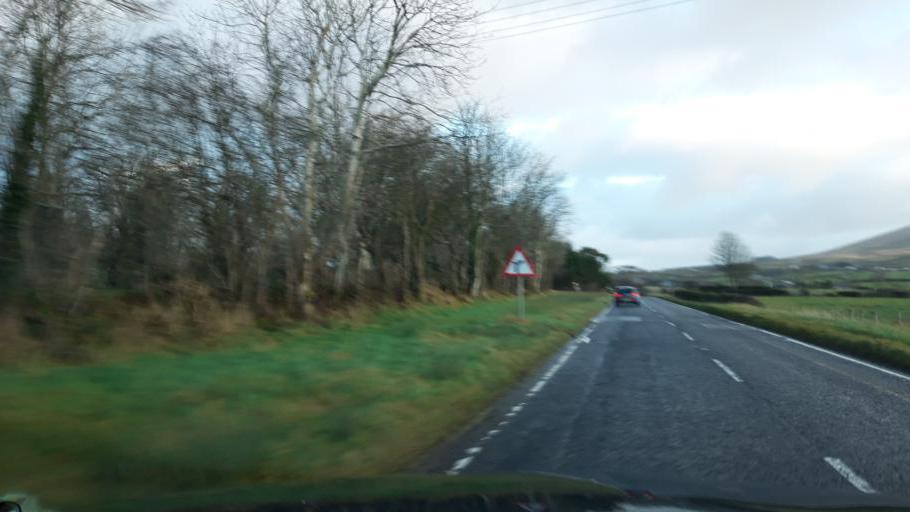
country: GB
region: Northern Ireland
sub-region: Moyle District
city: Ballycastle
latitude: 55.1424
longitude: -6.3197
